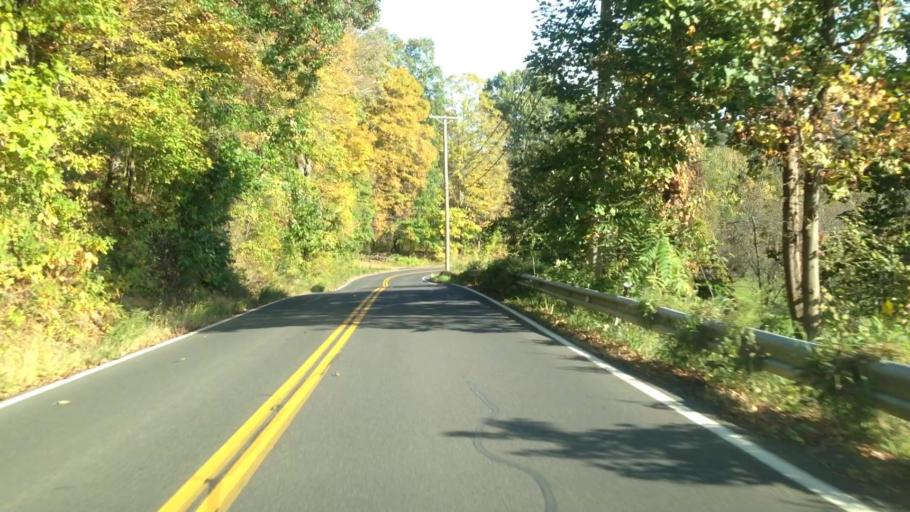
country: US
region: New York
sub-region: Dutchess County
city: Hyde Park
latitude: 41.8252
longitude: -73.9719
